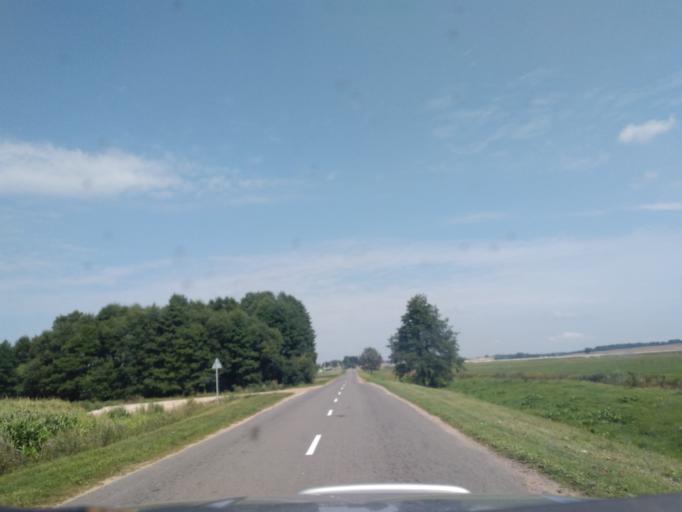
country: BY
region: Minsk
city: Valozhyn
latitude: 54.0335
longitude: 26.6047
